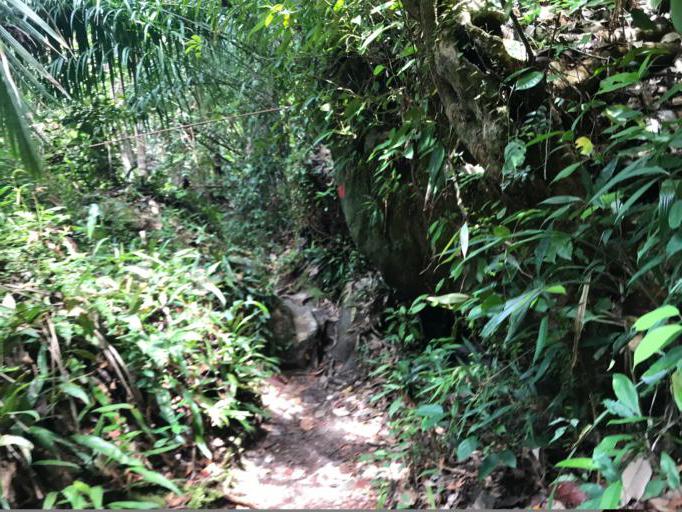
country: MY
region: Sarawak
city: Kuching
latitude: 1.7210
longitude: 110.4474
